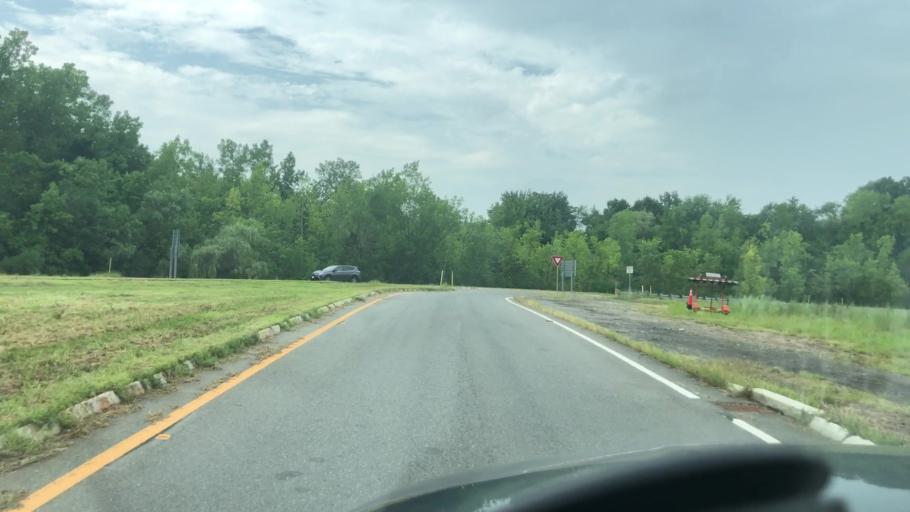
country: US
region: Massachusetts
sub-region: Hampden County
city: Holyoke
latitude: 42.2014
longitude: -72.6401
